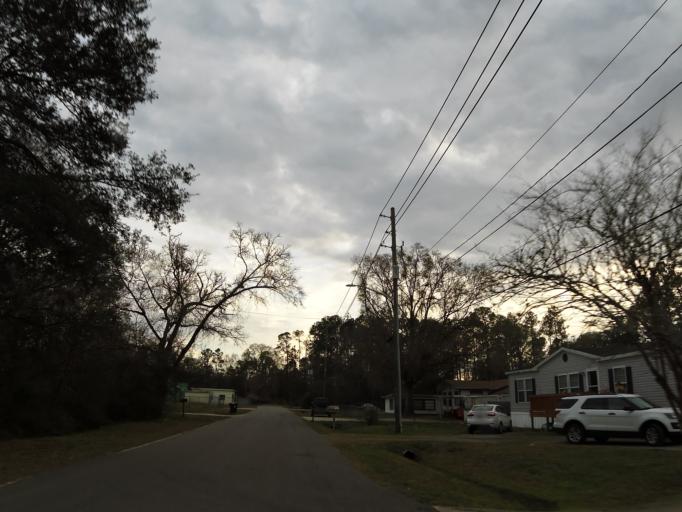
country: US
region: Florida
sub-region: Duval County
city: Baldwin
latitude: 30.2973
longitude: -81.9787
